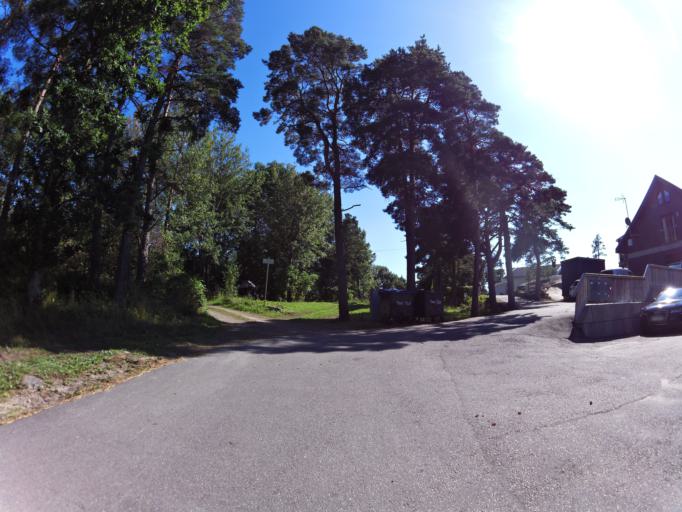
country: NO
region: Ostfold
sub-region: Fredrikstad
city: Fredrikstad
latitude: 59.1708
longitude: 10.8503
